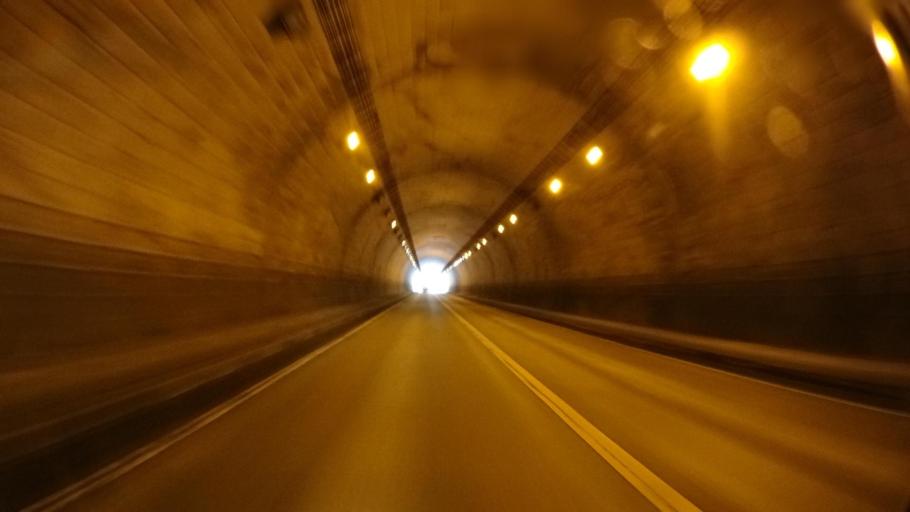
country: JP
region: Kyoto
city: Maizuru
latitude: 35.4667
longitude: 135.3737
